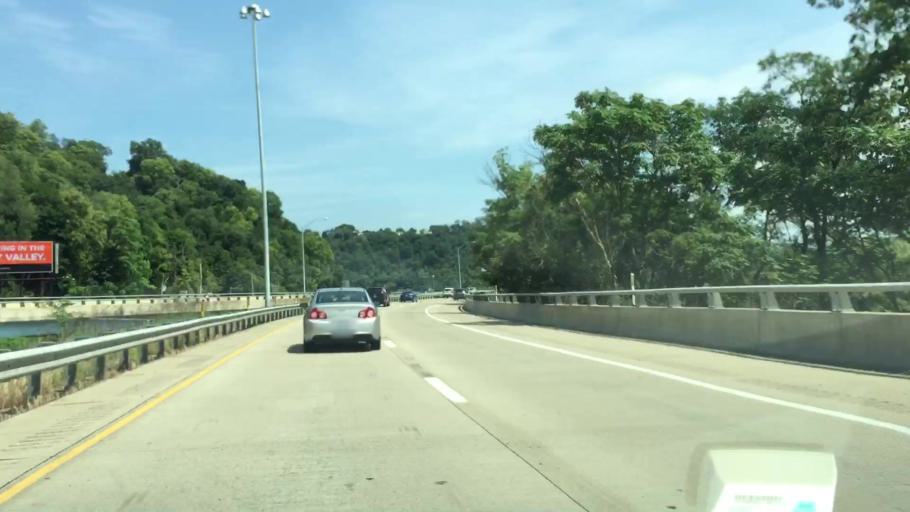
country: US
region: Pennsylvania
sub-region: Allegheny County
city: Etna
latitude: 40.4904
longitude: -79.9498
